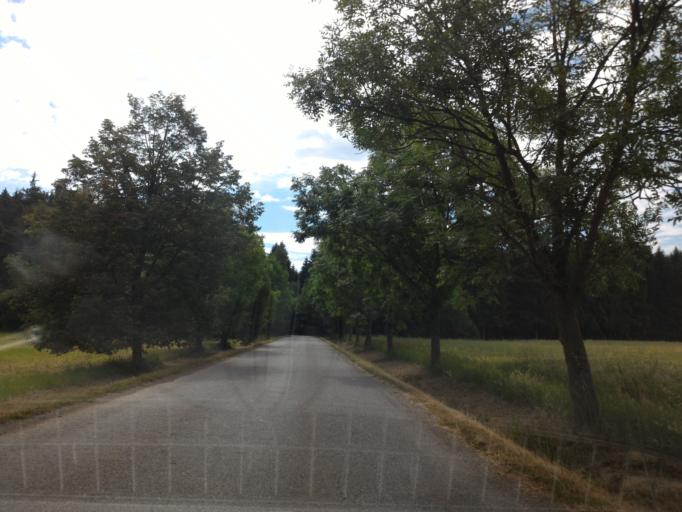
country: CZ
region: Vysocina
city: Zeletava
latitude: 49.1309
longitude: 15.5779
